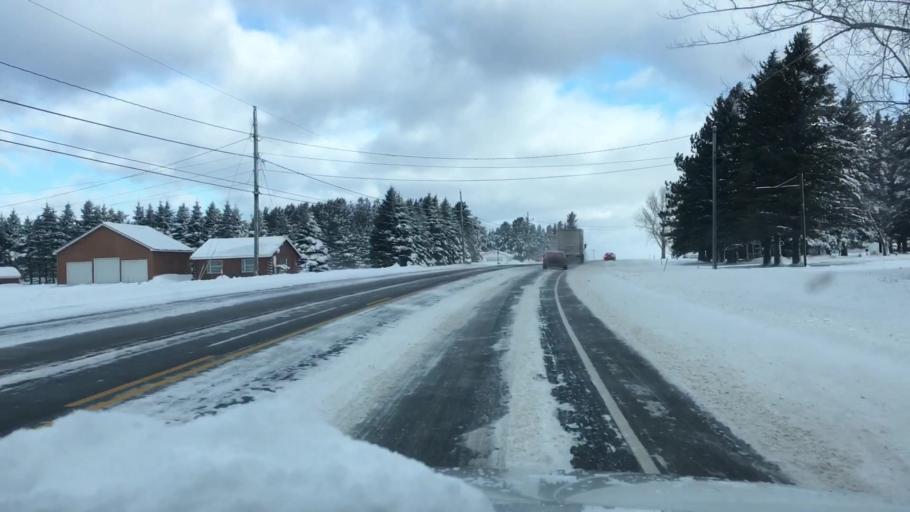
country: US
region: Maine
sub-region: Aroostook County
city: Caribou
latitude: 46.7909
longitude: -67.9912
